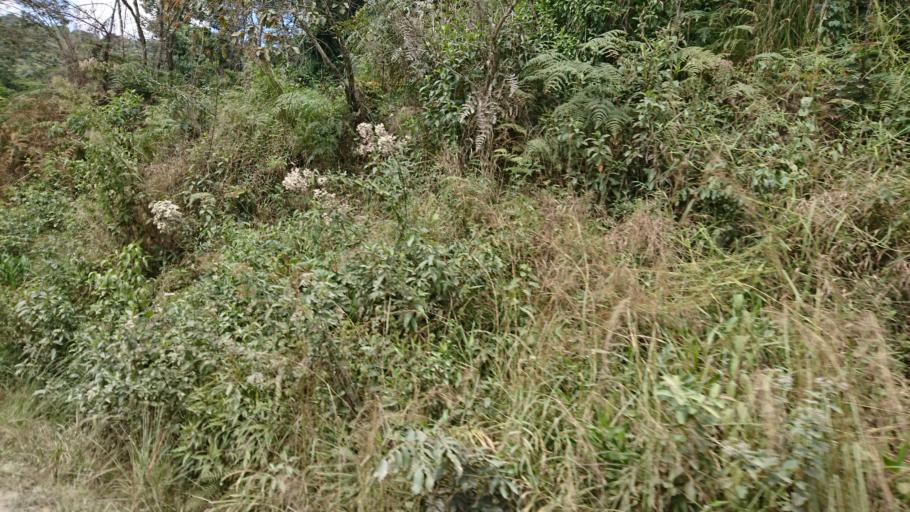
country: BO
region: La Paz
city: Coroico
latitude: -16.1127
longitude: -67.7724
